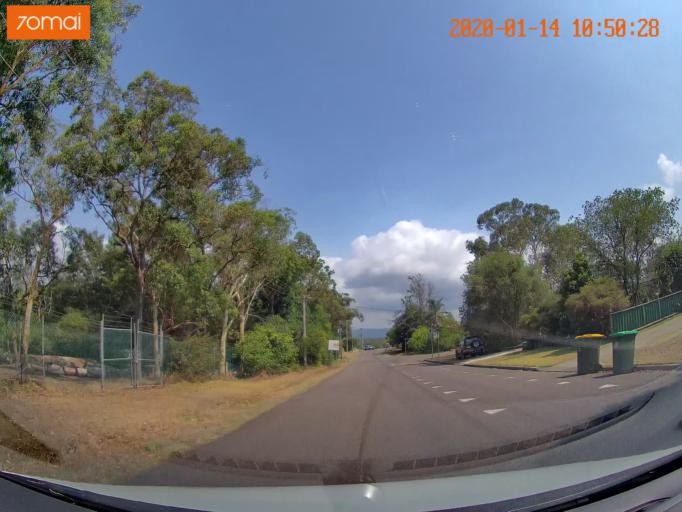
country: AU
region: New South Wales
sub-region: Lake Macquarie Shire
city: Dora Creek
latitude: -33.1030
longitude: 151.4869
